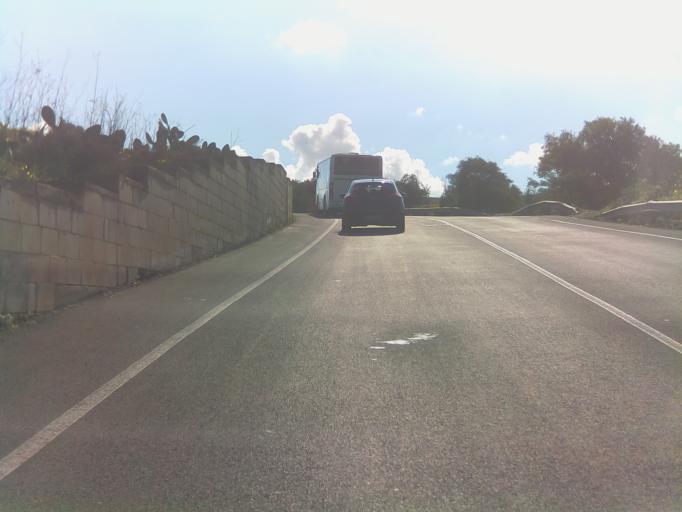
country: MT
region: L-Imgarr
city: Imgarr
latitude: 35.9285
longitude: 14.3528
